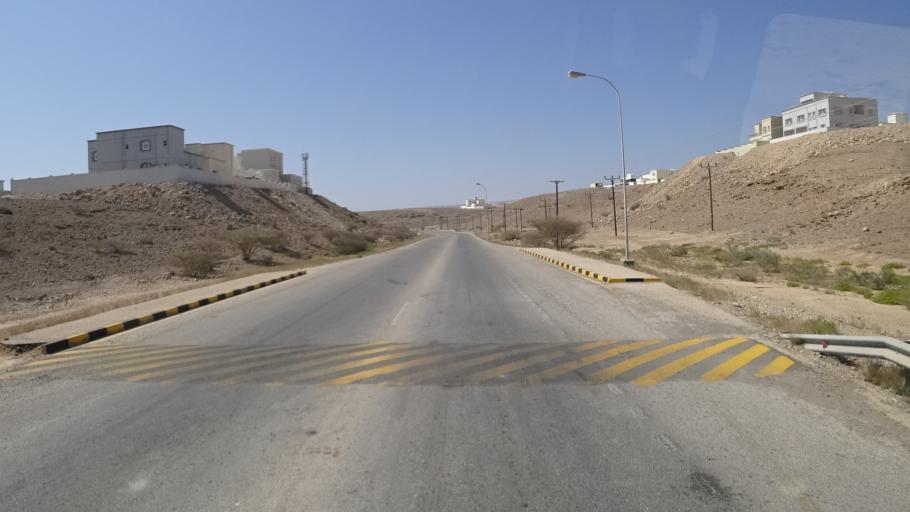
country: OM
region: Ash Sharqiyah
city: Sur
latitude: 22.5521
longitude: 59.4985
